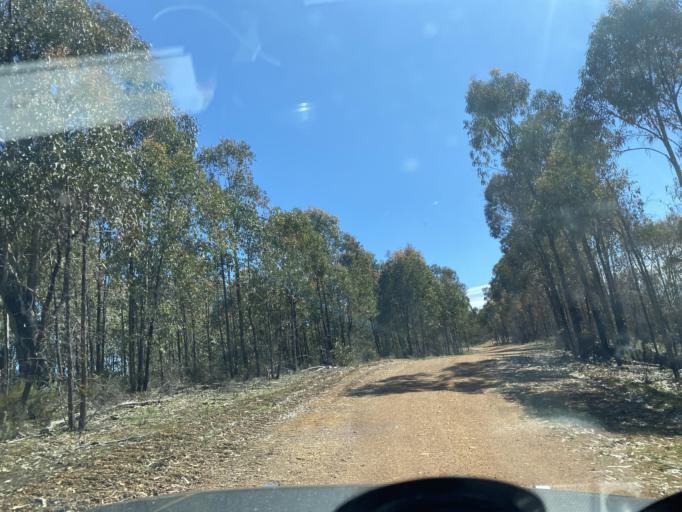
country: AU
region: Victoria
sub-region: Benalla
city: Benalla
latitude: -36.7355
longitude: 146.1821
